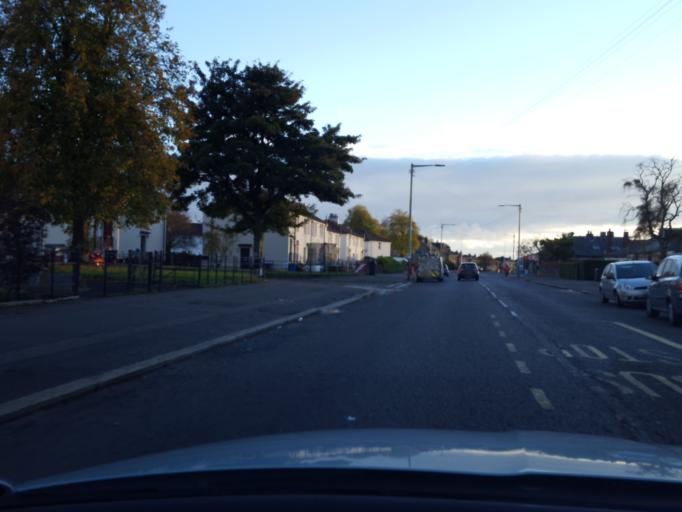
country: GB
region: Scotland
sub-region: Dundee City
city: Dundee
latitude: 56.4736
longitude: -2.9943
